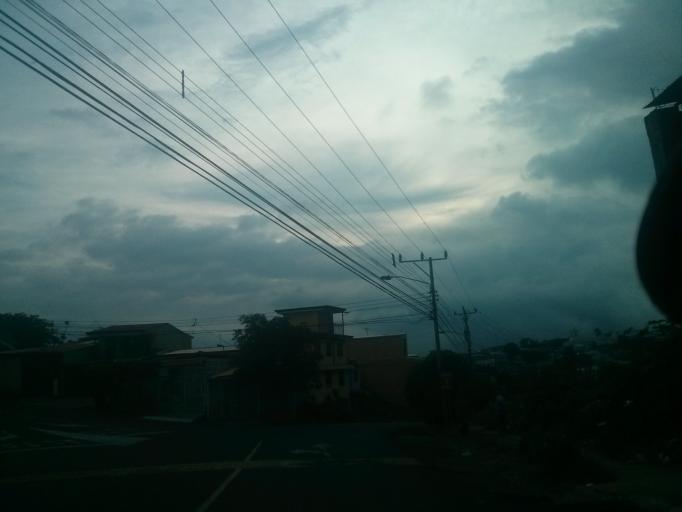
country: CR
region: Heredia
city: Heredia
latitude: 9.9942
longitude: -84.1100
